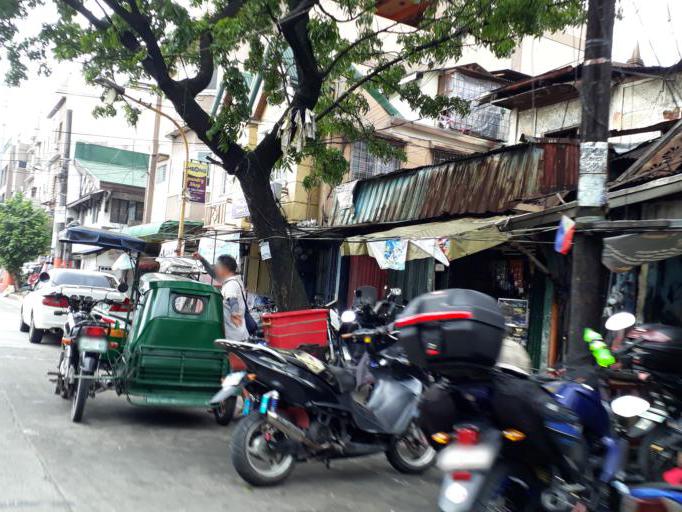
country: PH
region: Metro Manila
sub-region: City of Manila
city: Manila
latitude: 14.6182
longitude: 120.9943
